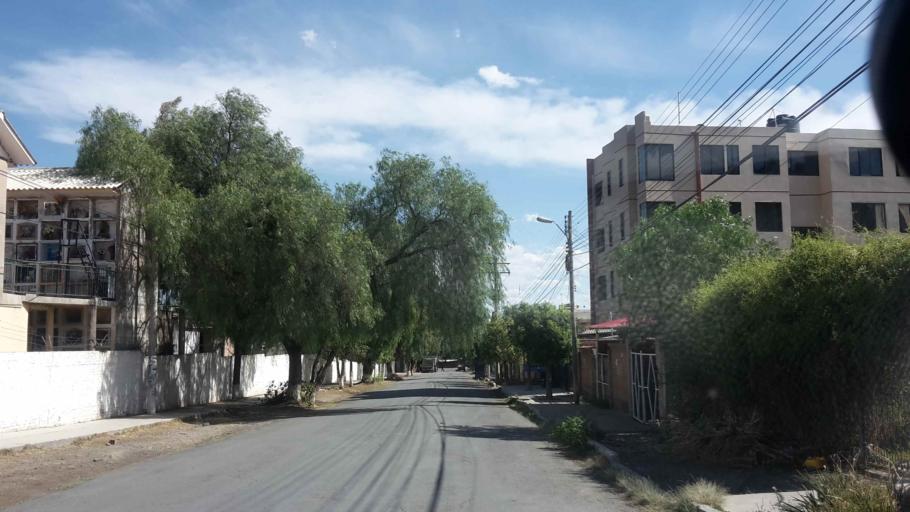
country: BO
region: Cochabamba
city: Cochabamba
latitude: -17.3344
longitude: -66.2262
